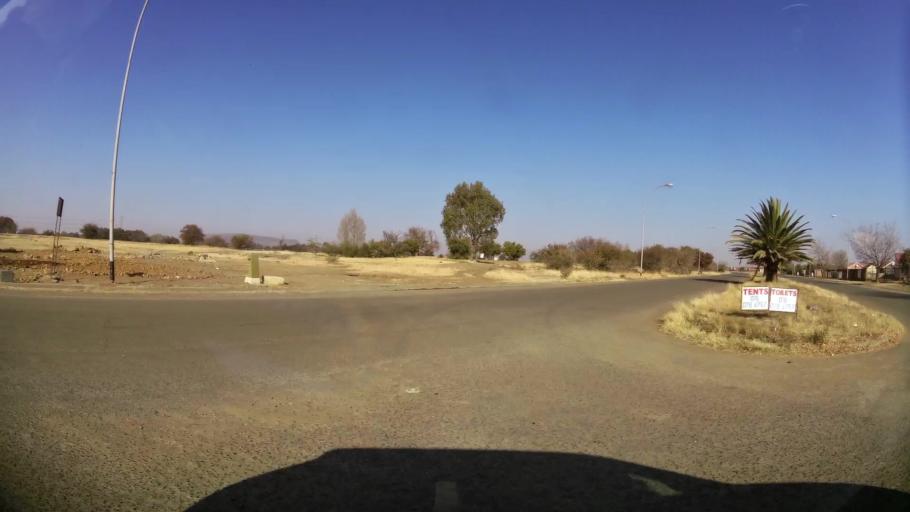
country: ZA
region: Orange Free State
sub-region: Mangaung Metropolitan Municipality
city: Bloemfontein
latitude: -29.1852
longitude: 26.1802
